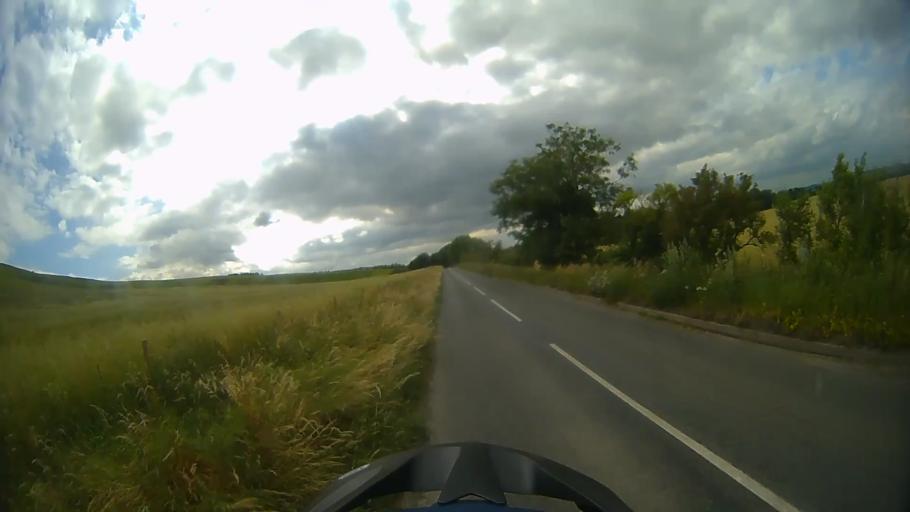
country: GB
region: England
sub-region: Oxfordshire
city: Faringdon
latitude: 51.5832
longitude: -1.5673
